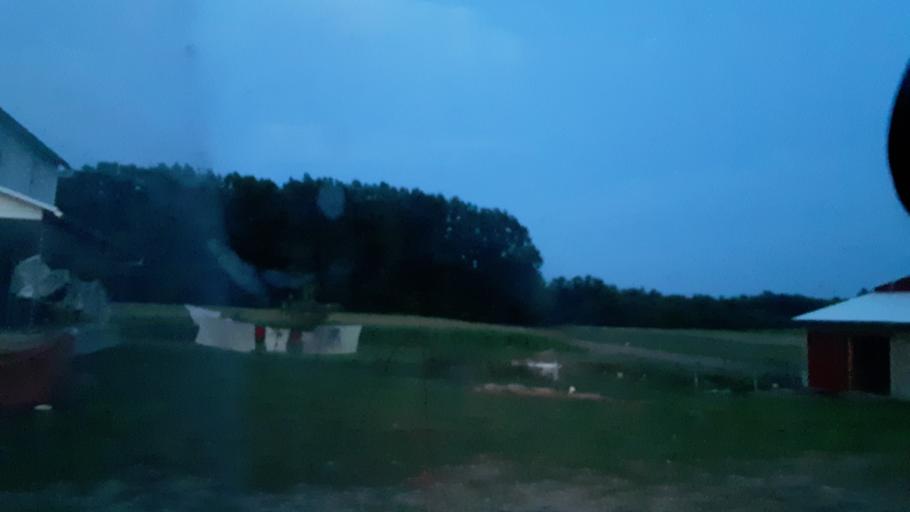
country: US
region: Ohio
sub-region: Wayne County
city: West Salem
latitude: 41.0220
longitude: -82.2010
